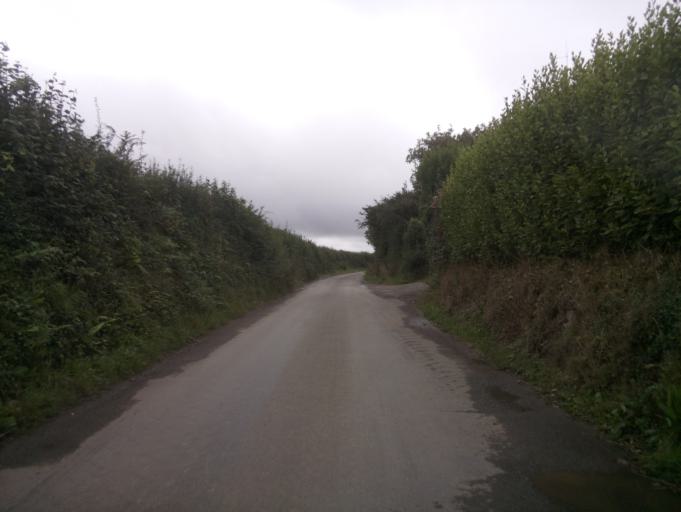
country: GB
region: England
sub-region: Devon
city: Kingsbridge
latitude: 50.3088
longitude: -3.7161
